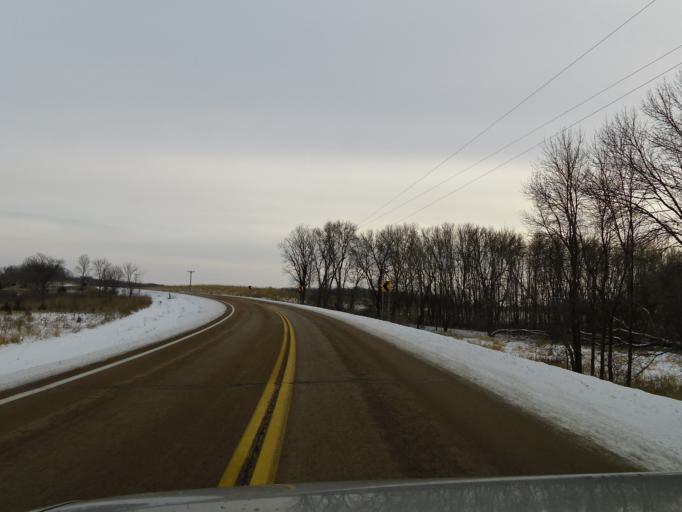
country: US
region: Minnesota
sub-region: Carver County
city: Victoria
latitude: 44.8816
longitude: -93.7026
